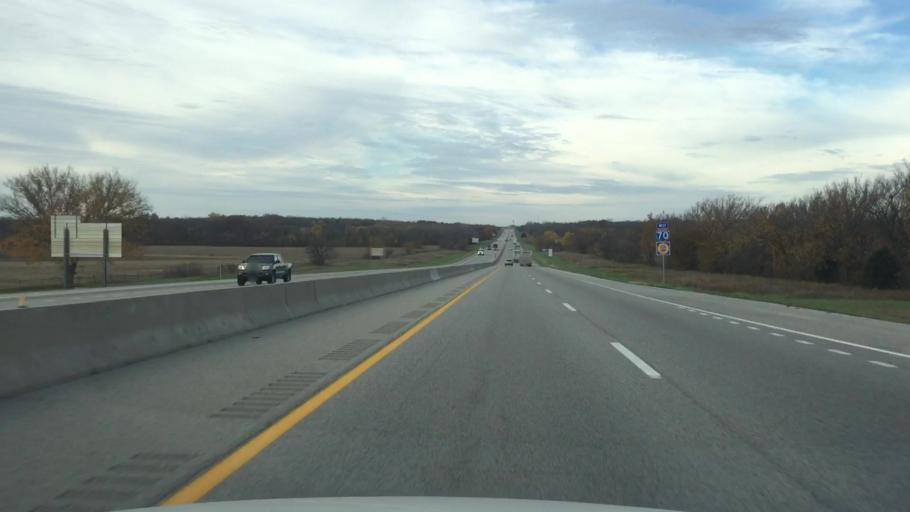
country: US
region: Kansas
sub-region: Leavenworth County
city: Tonganoxie
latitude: 39.0403
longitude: -95.1001
